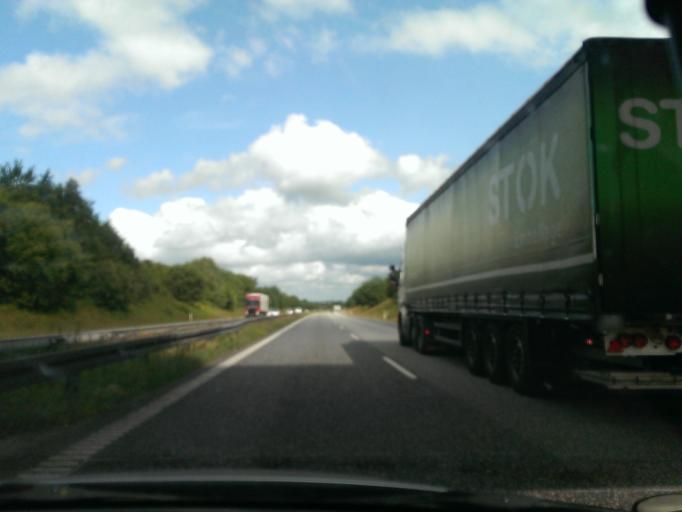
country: DK
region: North Denmark
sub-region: Mariagerfjord Kommune
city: Hobro
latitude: 56.6850
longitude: 9.7311
